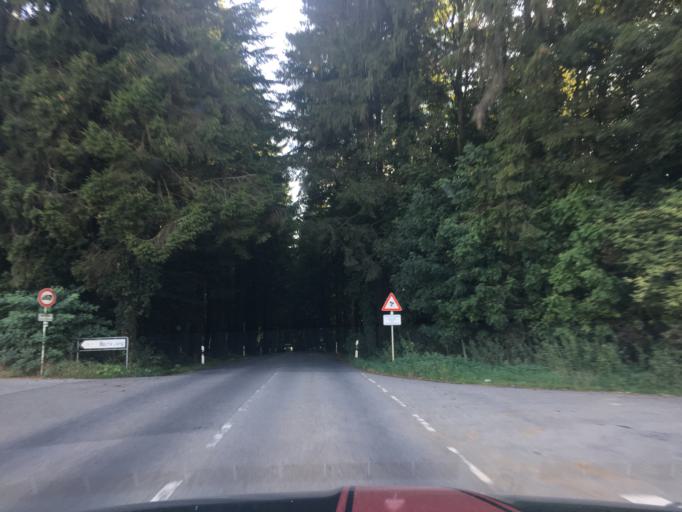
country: FR
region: Lorraine
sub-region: Departement de Meurthe-et-Moselle
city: Hussigny-Godbrange
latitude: 49.5049
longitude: 5.8677
